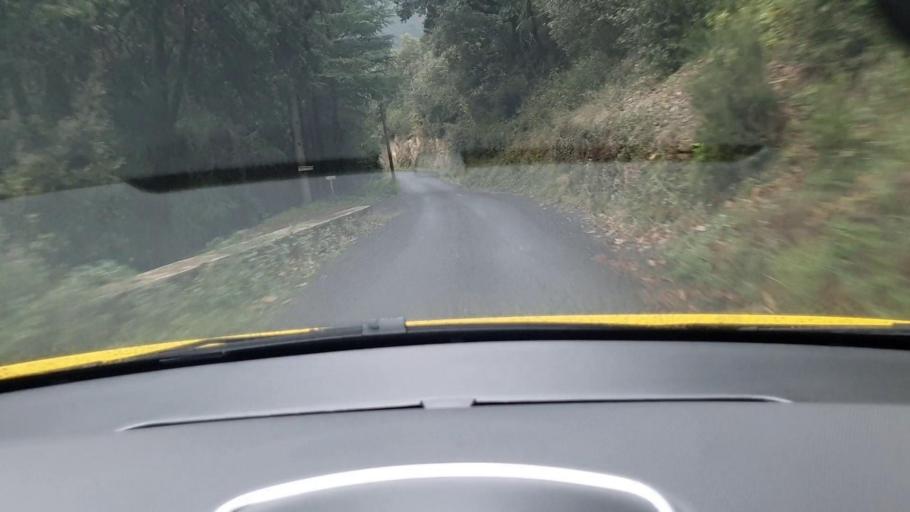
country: FR
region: Languedoc-Roussillon
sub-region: Departement du Gard
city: Sumene
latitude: 44.0242
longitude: 3.7308
